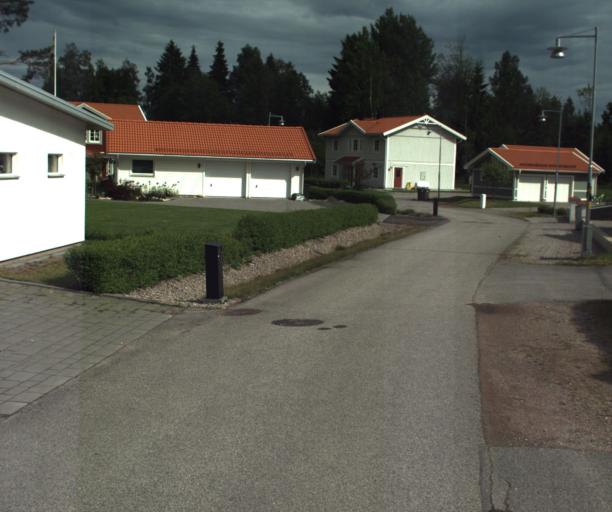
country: SE
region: Gaevleborg
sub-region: Gavle Kommun
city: Valbo
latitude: 60.6771
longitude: 17.0736
